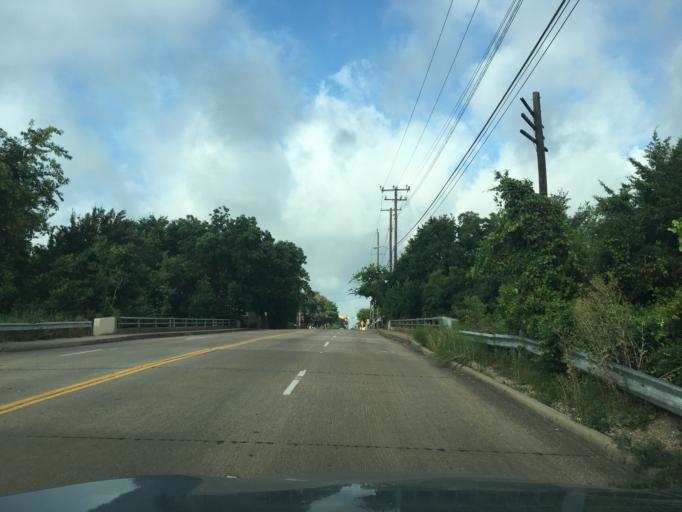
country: US
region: Texas
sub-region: Dallas County
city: University Park
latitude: 32.8769
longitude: -96.7533
